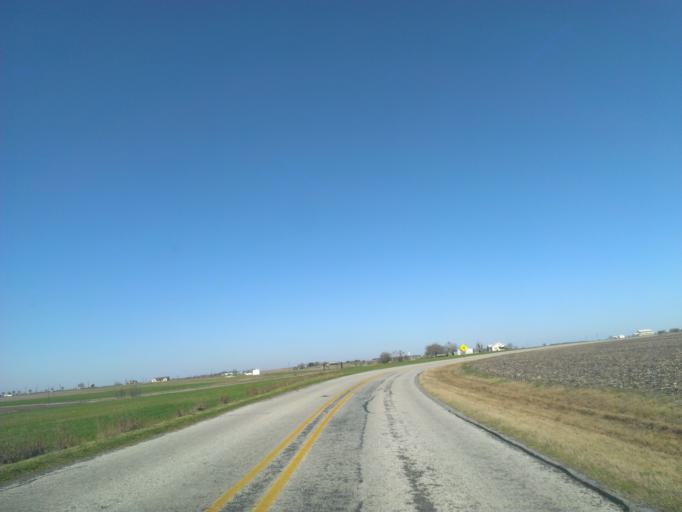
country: US
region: Texas
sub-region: Williamson County
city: Serenada
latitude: 30.7008
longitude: -97.5895
